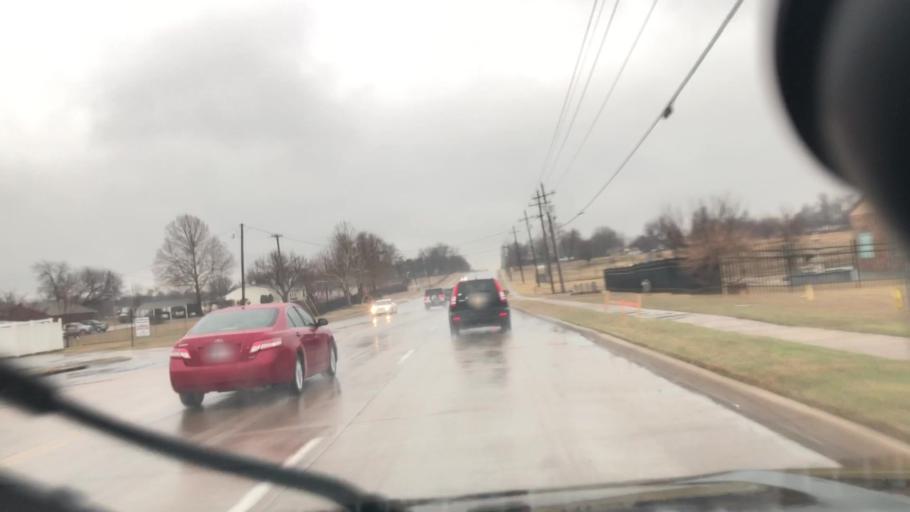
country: US
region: Oklahoma
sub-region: Rogers County
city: Catoosa
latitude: 36.1470
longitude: -95.8334
